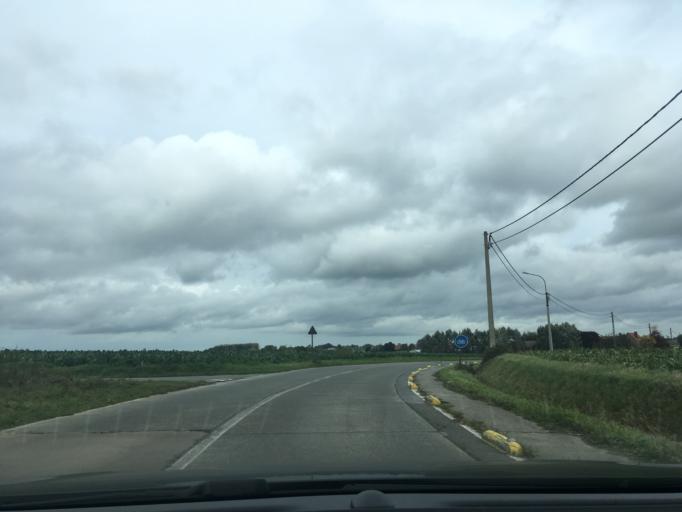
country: BE
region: Flanders
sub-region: Provincie West-Vlaanderen
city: Moorslede
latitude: 50.8618
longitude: 3.0313
